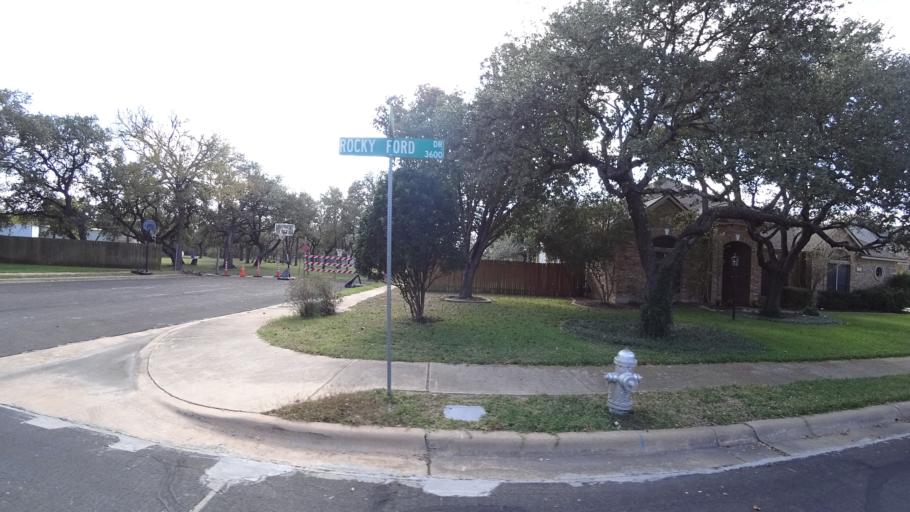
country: US
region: Texas
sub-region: Travis County
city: Shady Hollow
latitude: 30.1788
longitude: -97.8555
